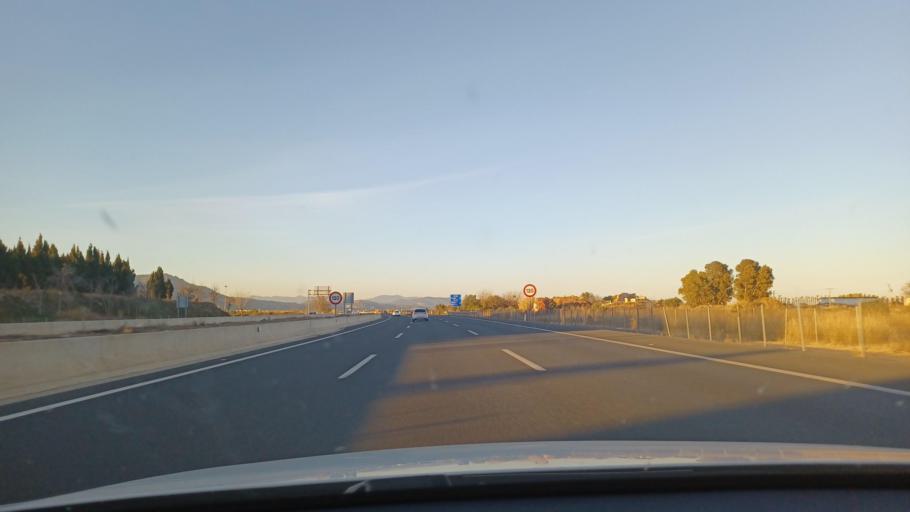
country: ES
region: Valencia
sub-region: Provincia de Valencia
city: Puig
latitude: 39.5928
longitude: -0.2930
